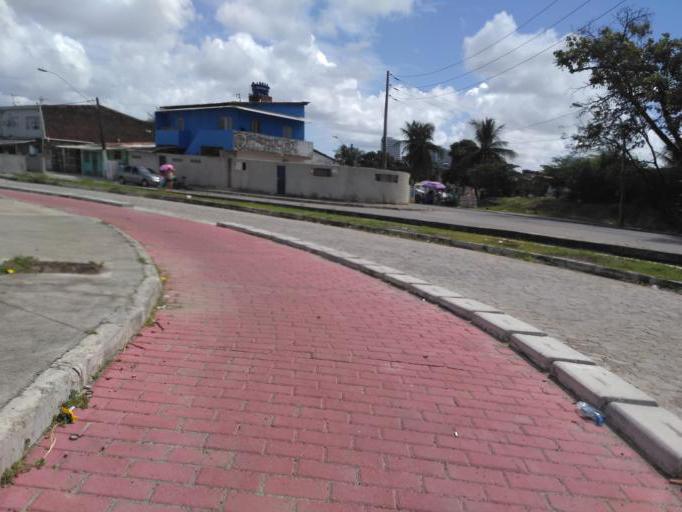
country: BR
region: Pernambuco
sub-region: Recife
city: Recife
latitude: -8.0725
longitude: -34.8967
